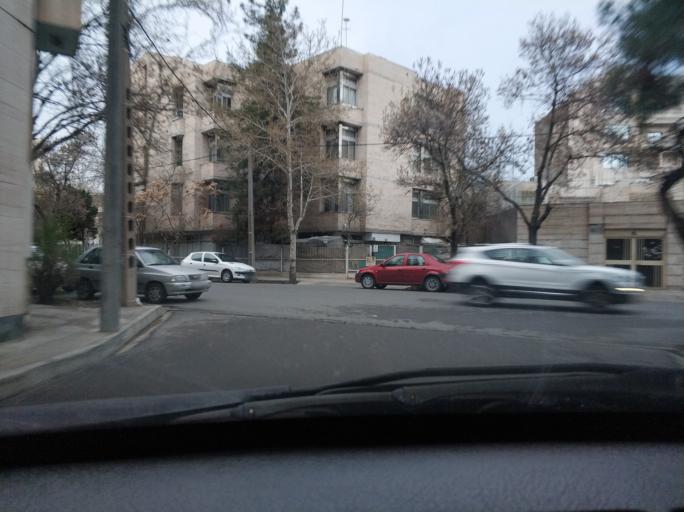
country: IR
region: Razavi Khorasan
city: Mashhad
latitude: 36.2755
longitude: 59.5940
